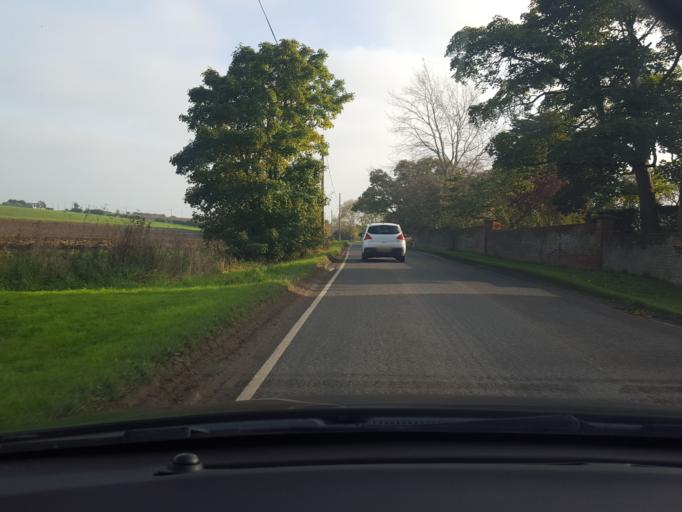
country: GB
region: England
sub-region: Essex
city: Little Clacton
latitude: 51.8640
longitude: 1.1842
